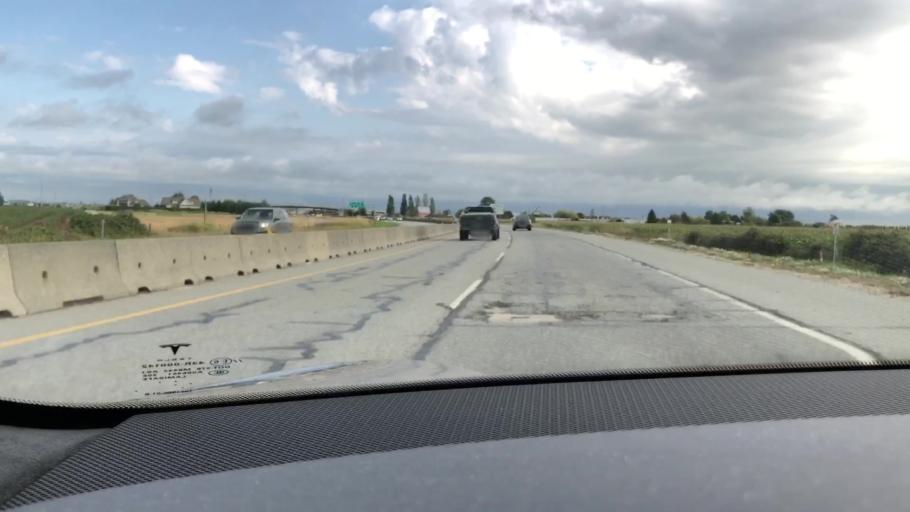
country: CA
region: British Columbia
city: Ladner
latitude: 49.0482
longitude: -123.0591
